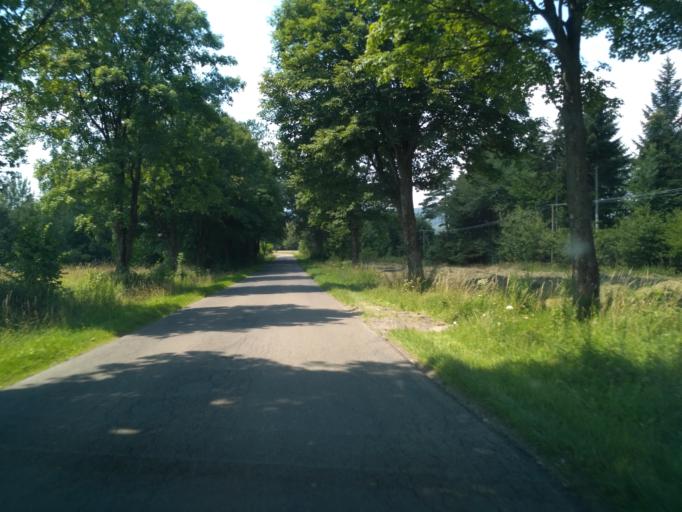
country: PL
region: Subcarpathian Voivodeship
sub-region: Powiat strzyzowski
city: Jawornik
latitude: 49.8726
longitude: 21.8502
